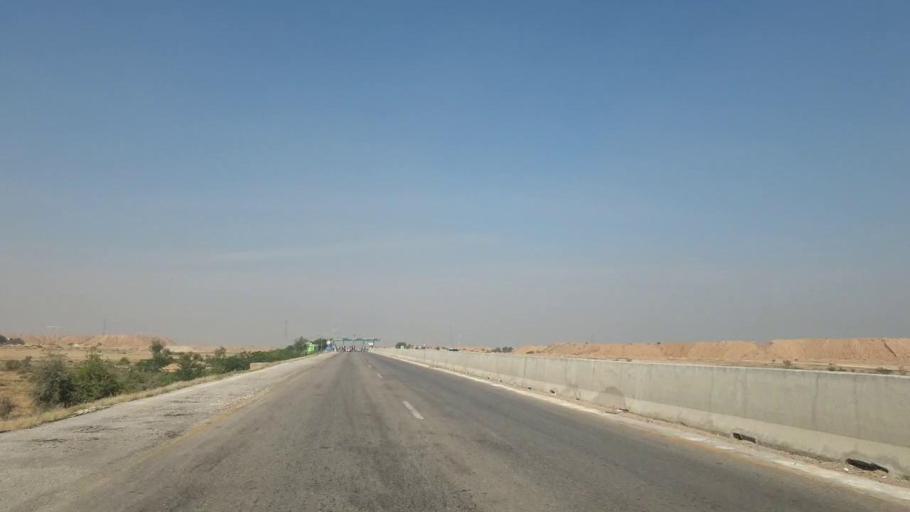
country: PK
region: Sindh
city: Matiari
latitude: 25.5753
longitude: 68.3142
